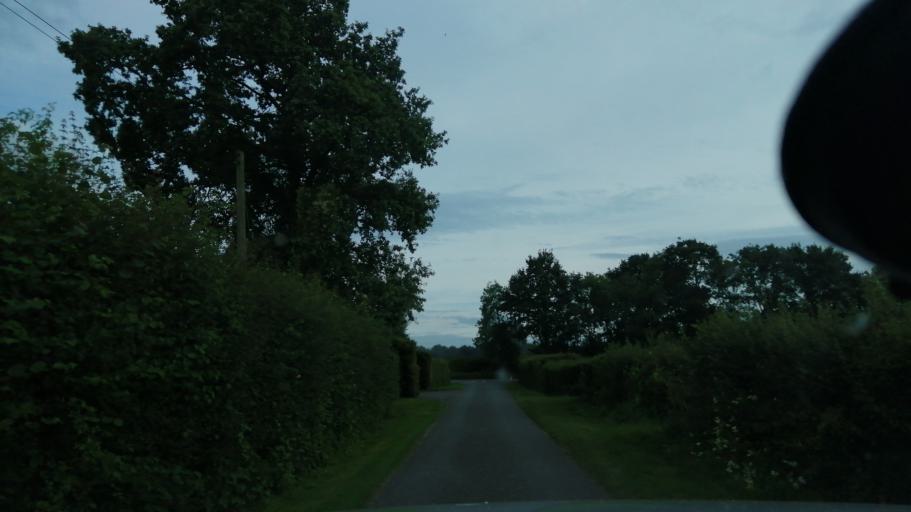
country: GB
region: England
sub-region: Herefordshire
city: Thruxton
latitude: 52.0077
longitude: -2.7970
